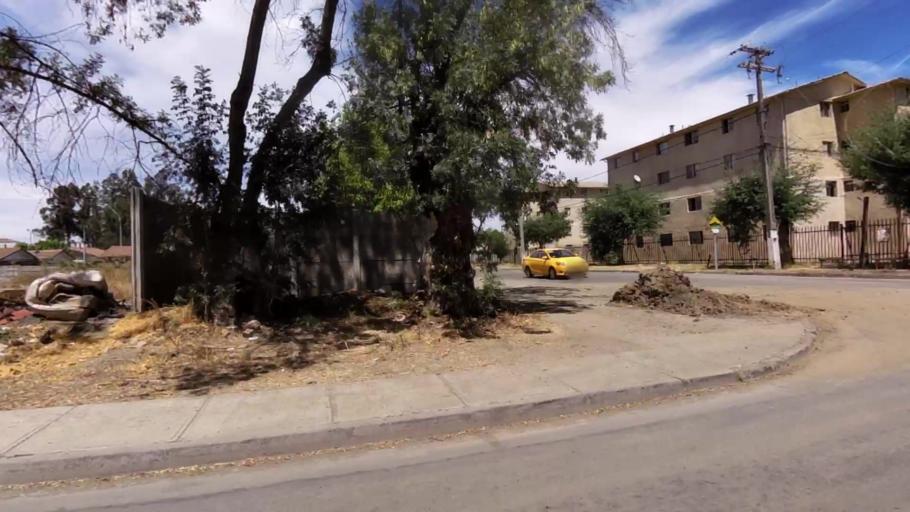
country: CL
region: O'Higgins
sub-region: Provincia de Cachapoal
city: Graneros
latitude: -34.0578
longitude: -70.7250
